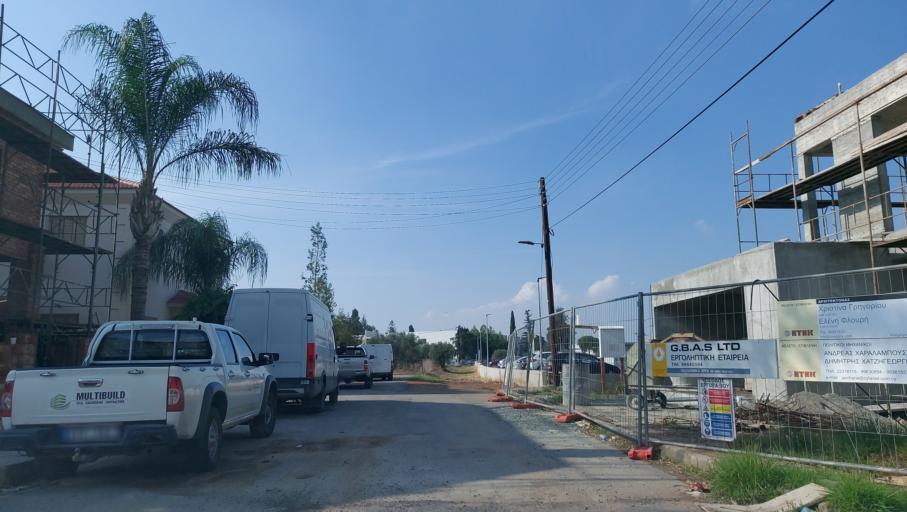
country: CY
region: Lefkosia
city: Tseri
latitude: 35.1091
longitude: 33.3087
